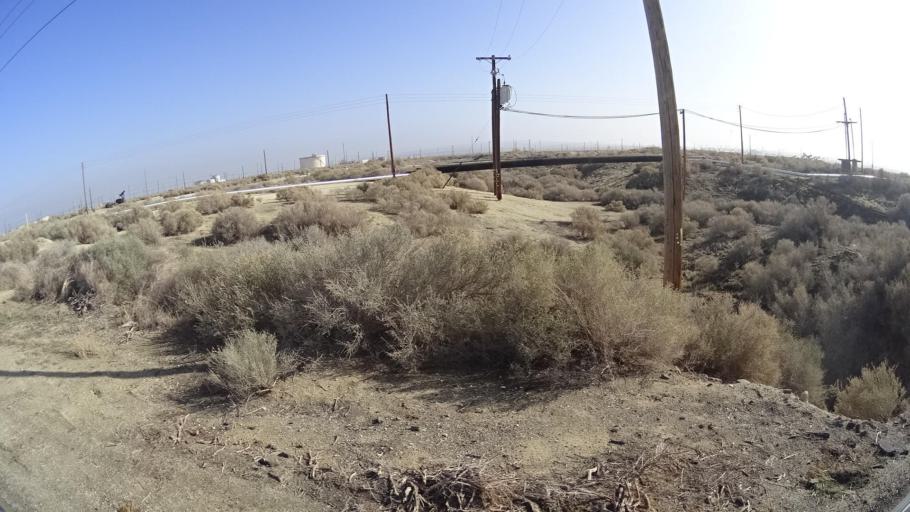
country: US
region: California
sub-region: Kern County
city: Taft Heights
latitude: 35.2149
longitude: -119.5697
